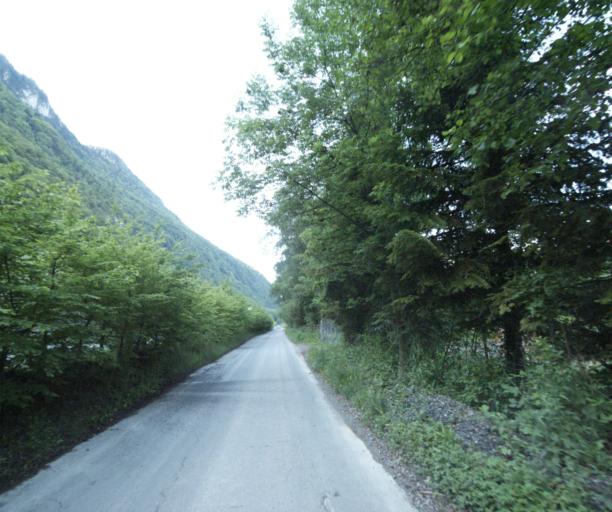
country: CH
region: Vaud
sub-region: Aigle District
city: Villeneuve
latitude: 46.3843
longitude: 6.9366
